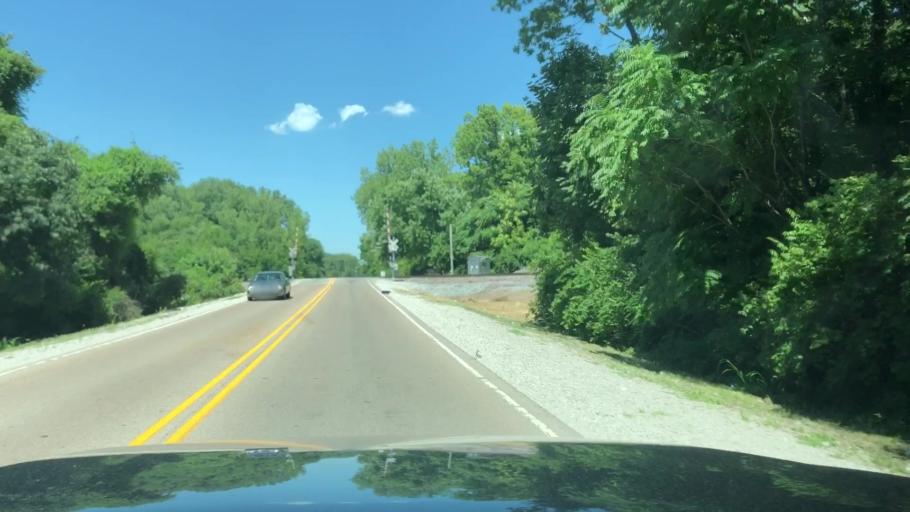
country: US
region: Illinois
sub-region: Saint Clair County
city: Centreville
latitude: 38.5626
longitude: -90.0962
